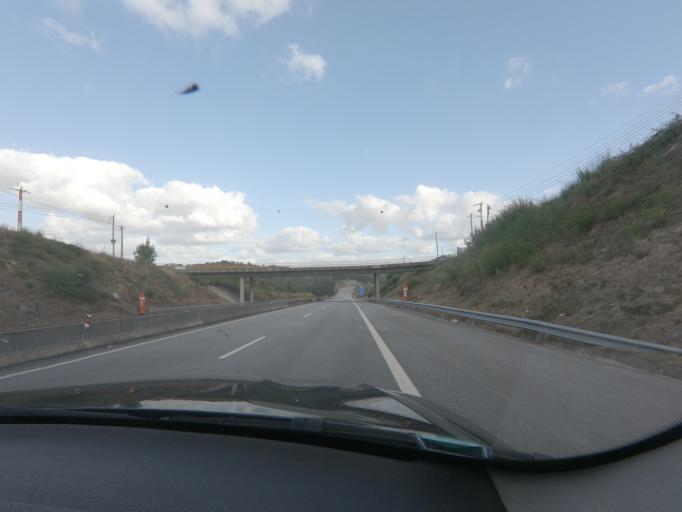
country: PT
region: Viseu
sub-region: Viseu
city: Abraveses
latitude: 40.6449
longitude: -7.9648
